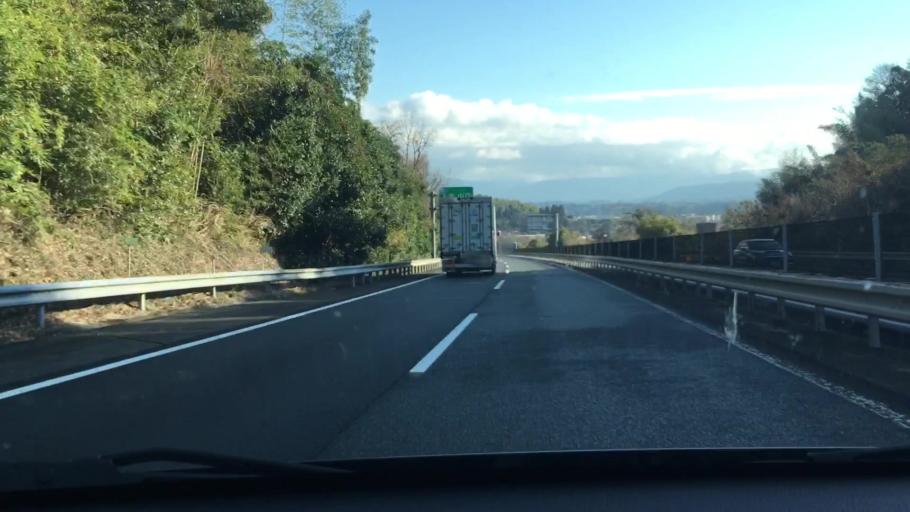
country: JP
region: Kumamoto
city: Hitoyoshi
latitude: 32.2396
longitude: 130.7608
